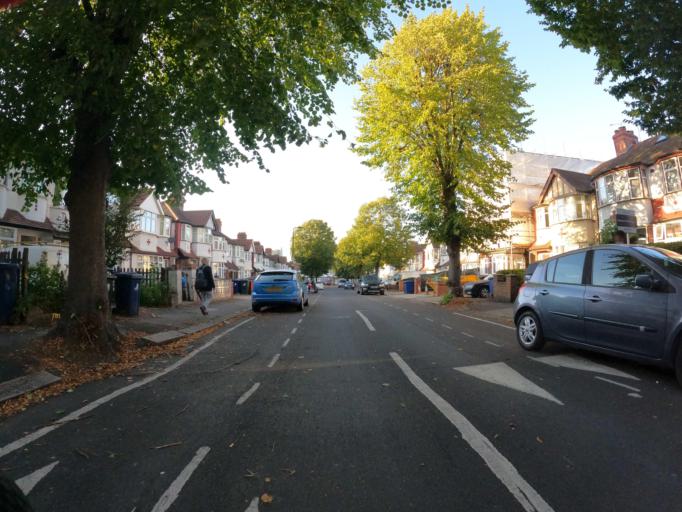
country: GB
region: England
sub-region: Greater London
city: Ealing Broadway
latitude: 51.5333
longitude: -0.2939
